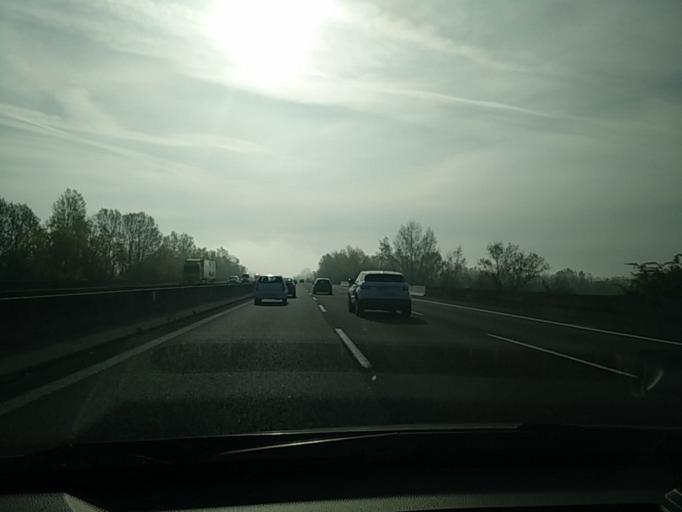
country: IT
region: Emilia-Romagna
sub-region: Provincia di Bologna
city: Ozzano dell'Emilia
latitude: 44.4603
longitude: 11.5058
